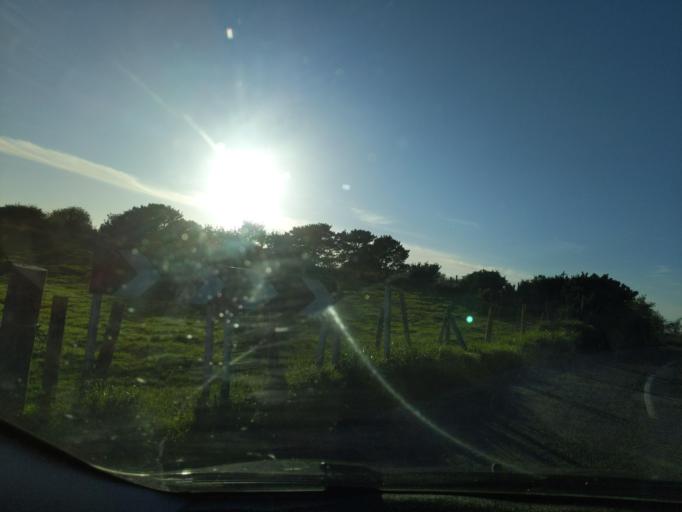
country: GB
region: England
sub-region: Plymouth
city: Plymstock
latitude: 50.3444
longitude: -4.1148
